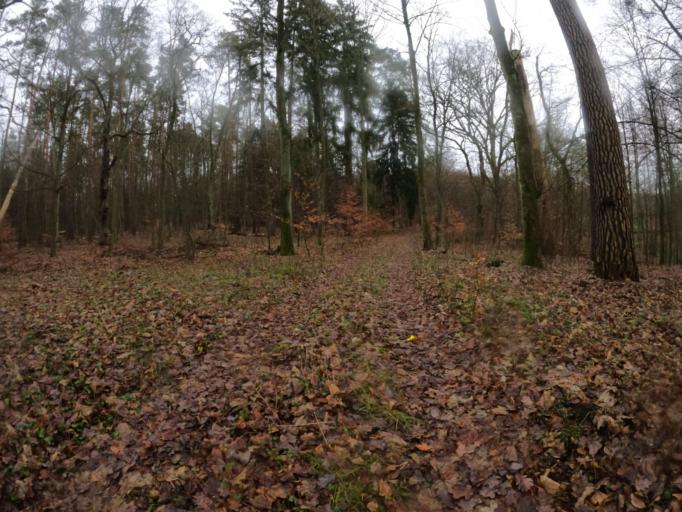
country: PL
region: West Pomeranian Voivodeship
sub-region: Powiat mysliborski
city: Debno
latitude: 52.7540
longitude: 14.7672
